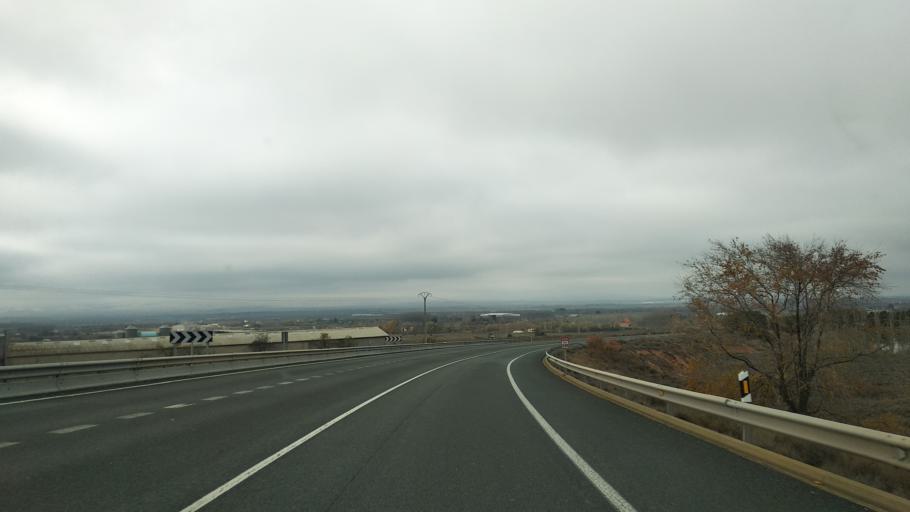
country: ES
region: La Rioja
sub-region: Provincia de La Rioja
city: Alfaro
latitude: 42.1611
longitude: -1.7431
